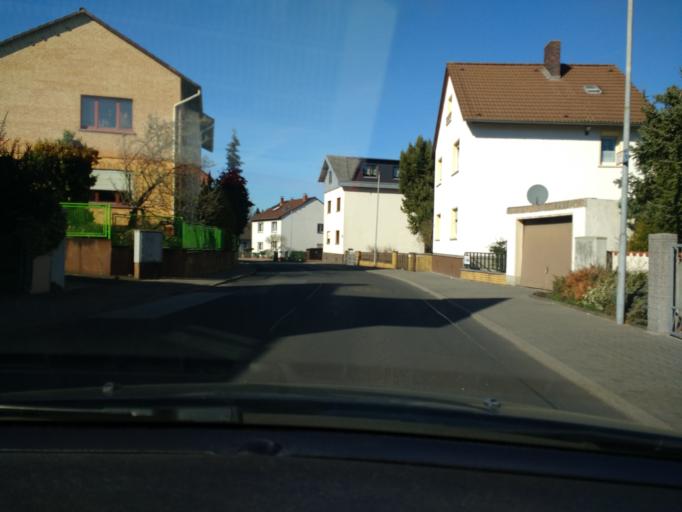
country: DE
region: Hesse
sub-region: Regierungsbezirk Darmstadt
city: Rodenbach
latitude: 50.1381
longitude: 9.0583
